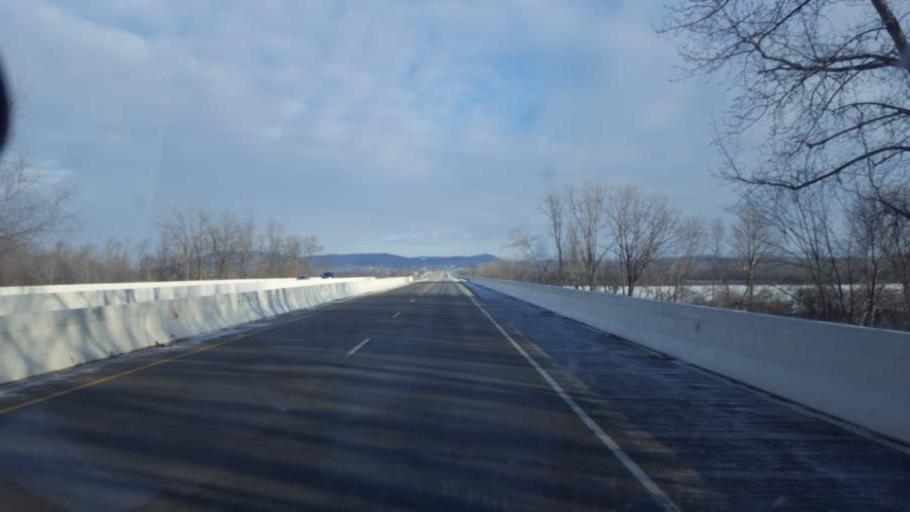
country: US
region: Ohio
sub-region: Ross County
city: Chillicothe
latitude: 39.3002
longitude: -82.9428
